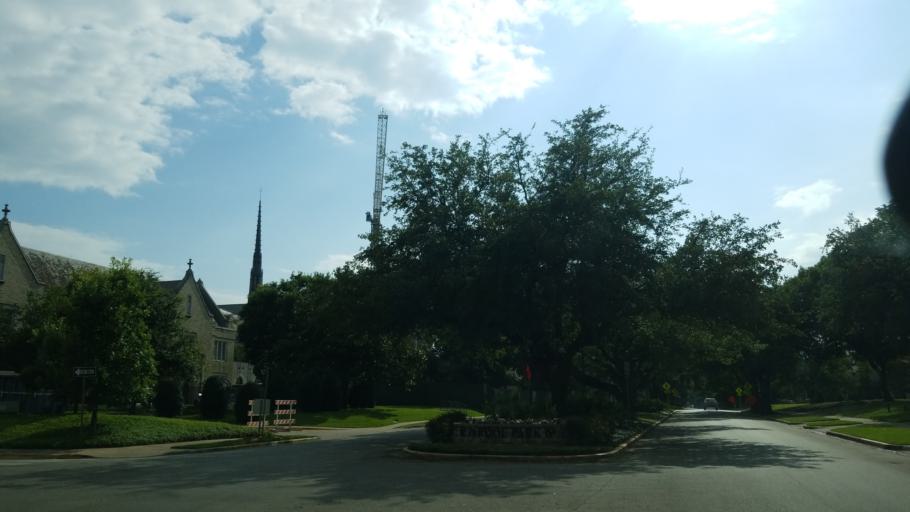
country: US
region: Texas
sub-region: Dallas County
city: University Park
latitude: 32.8454
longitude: -96.7987
